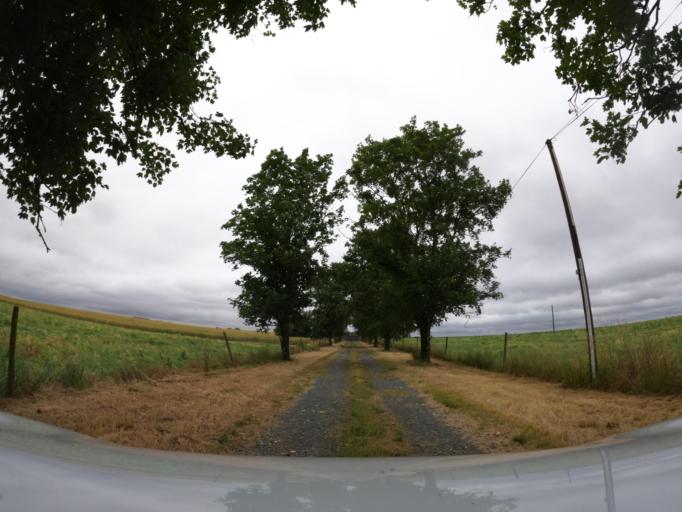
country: FR
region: Pays de la Loire
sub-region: Departement de la Vendee
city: Maillezais
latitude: 46.4071
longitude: -0.7198
